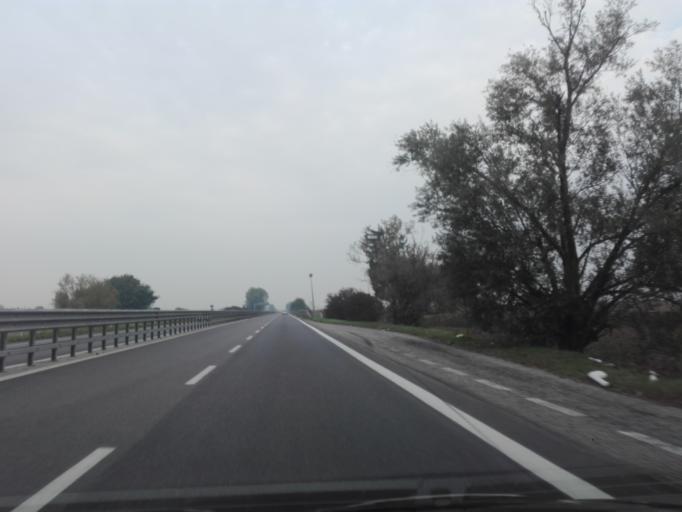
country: IT
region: Veneto
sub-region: Provincia di Rovigo
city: San Bellino
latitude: 45.0300
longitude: 11.5697
